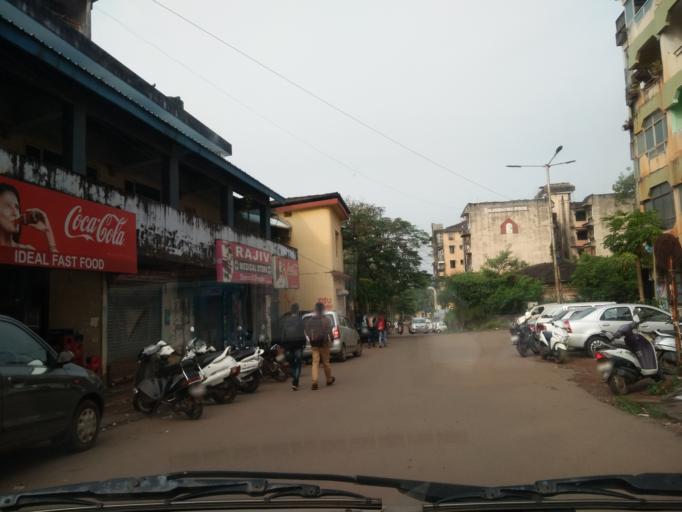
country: IN
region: Goa
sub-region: South Goa
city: Madgaon
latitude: 15.2734
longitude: 73.9555
